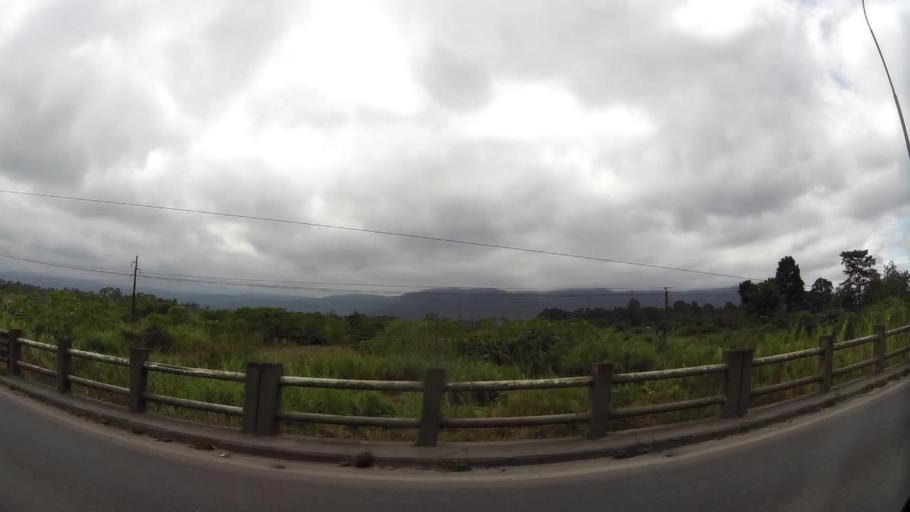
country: EC
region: Guayas
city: Naranjal
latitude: -2.6903
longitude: -79.6412
